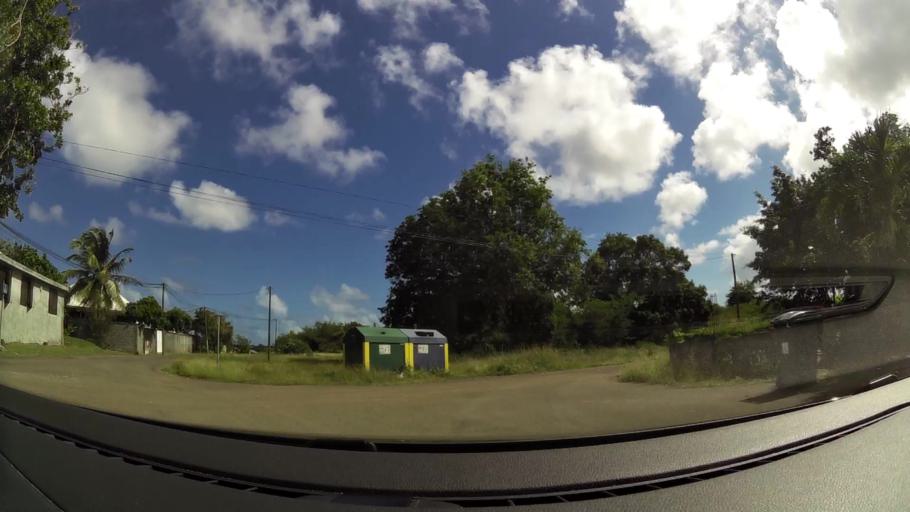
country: GP
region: Guadeloupe
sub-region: Guadeloupe
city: Anse-Bertrand
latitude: 16.4653
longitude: -61.5032
